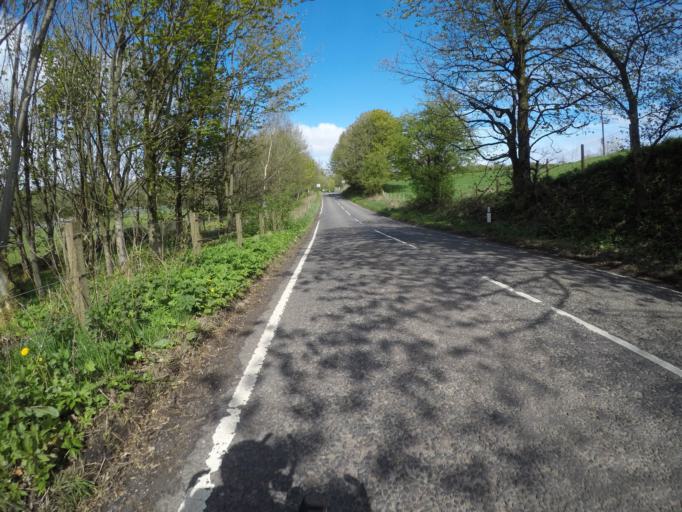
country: GB
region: Scotland
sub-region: East Ayrshire
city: Stewarton
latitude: 55.6749
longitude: -4.5222
